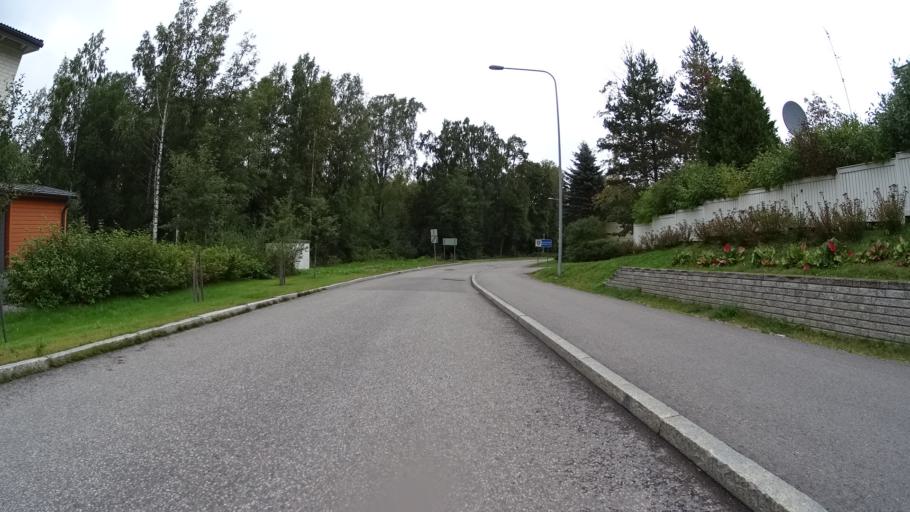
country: FI
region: Uusimaa
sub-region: Helsinki
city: Kauniainen
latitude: 60.2079
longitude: 24.7180
